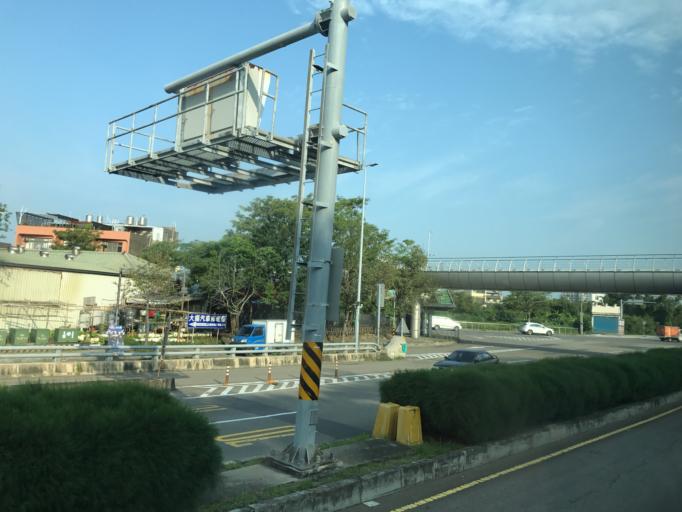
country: TW
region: Taiwan
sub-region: Hsinchu
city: Hsinchu
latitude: 24.7975
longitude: 120.9491
